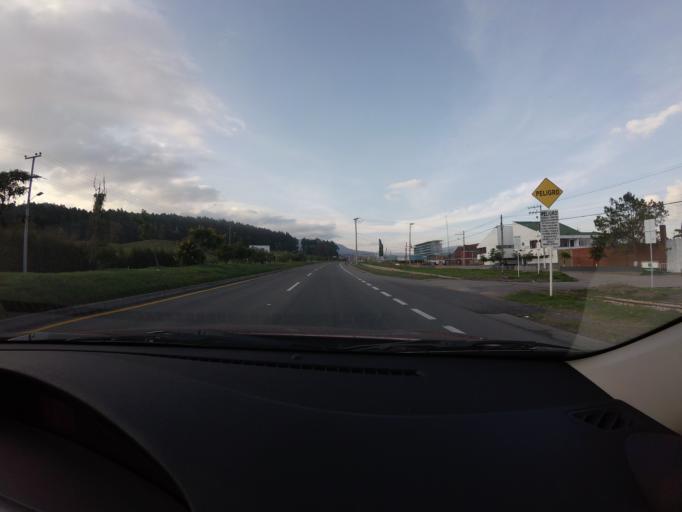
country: CO
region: Cundinamarca
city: Zipaquira
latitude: 5.0126
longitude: -74.0051
